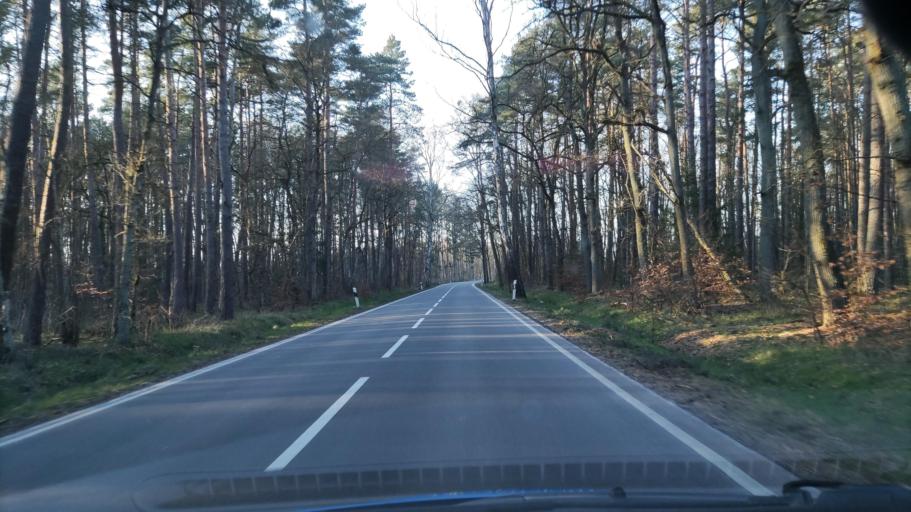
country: DE
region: Brandenburg
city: Lanz
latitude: 53.0033
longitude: 11.5511
